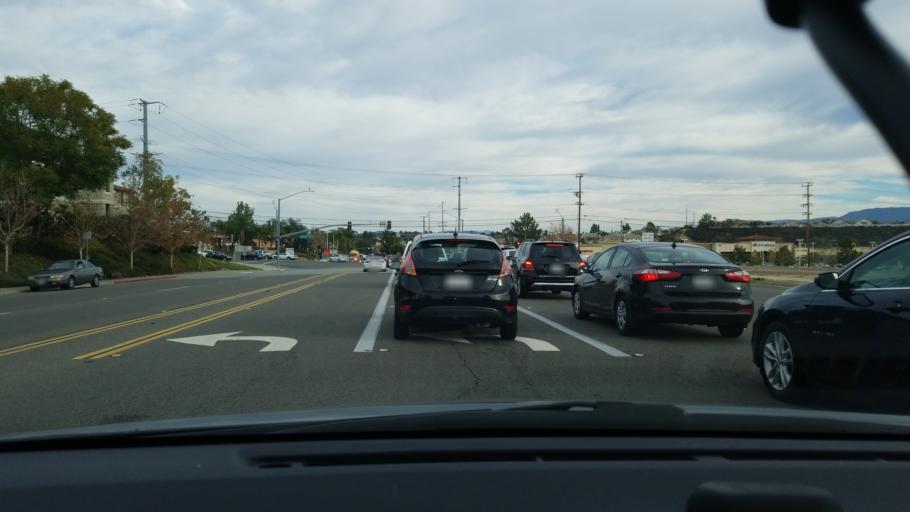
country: US
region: California
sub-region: Riverside County
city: Murrieta Hot Springs
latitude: 33.5529
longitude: -117.1419
